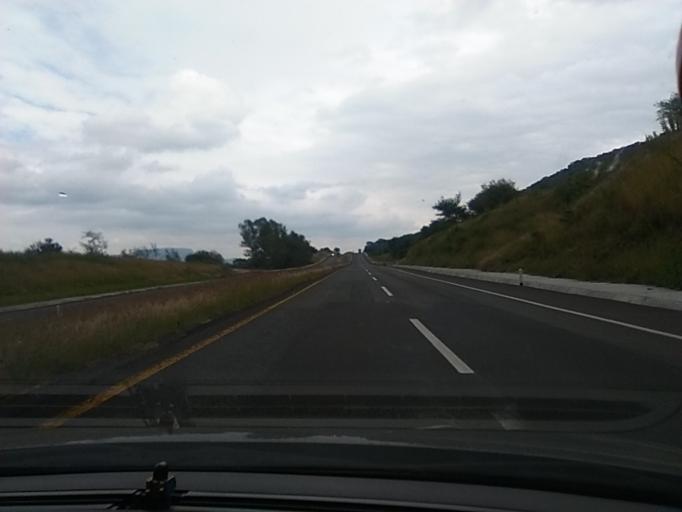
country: MX
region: Jalisco
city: Ocotlan
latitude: 20.4200
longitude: -102.7612
